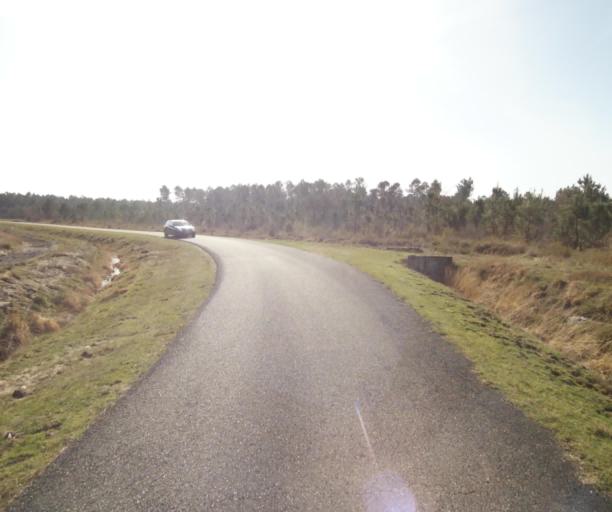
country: FR
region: Aquitaine
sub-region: Departement des Landes
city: Roquefort
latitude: 44.2100
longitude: -0.2499
